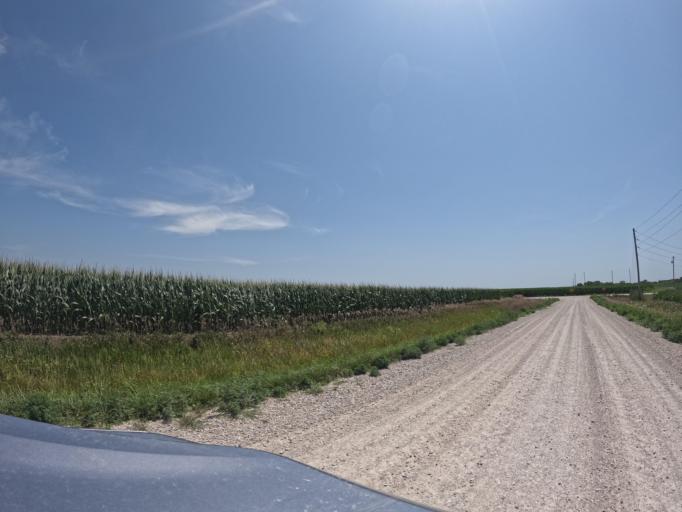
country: US
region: Iowa
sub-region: Henry County
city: Mount Pleasant
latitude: 40.9097
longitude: -91.6457
